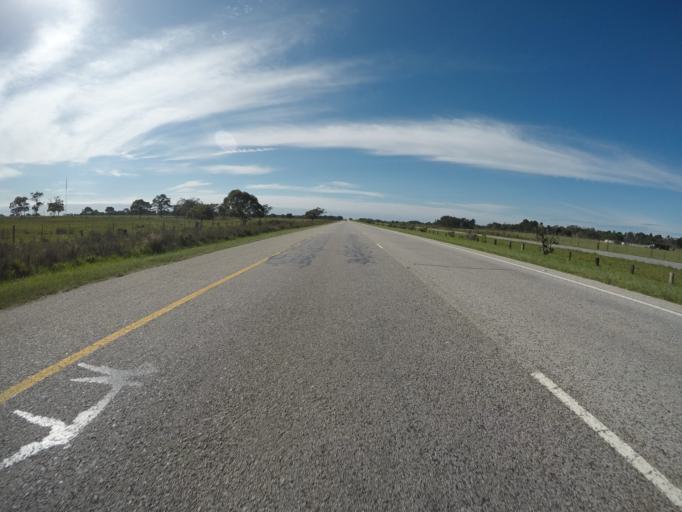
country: ZA
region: Eastern Cape
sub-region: Nelson Mandela Bay Metropolitan Municipality
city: Port Elizabeth
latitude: -33.9501
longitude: 25.4306
